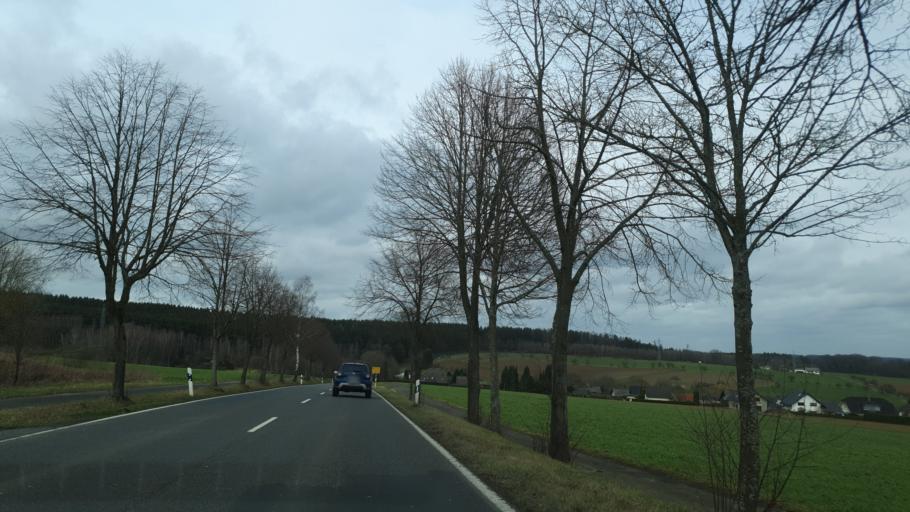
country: DE
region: Rheinland-Pfalz
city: Niederhofen
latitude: 50.5700
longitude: 7.5890
